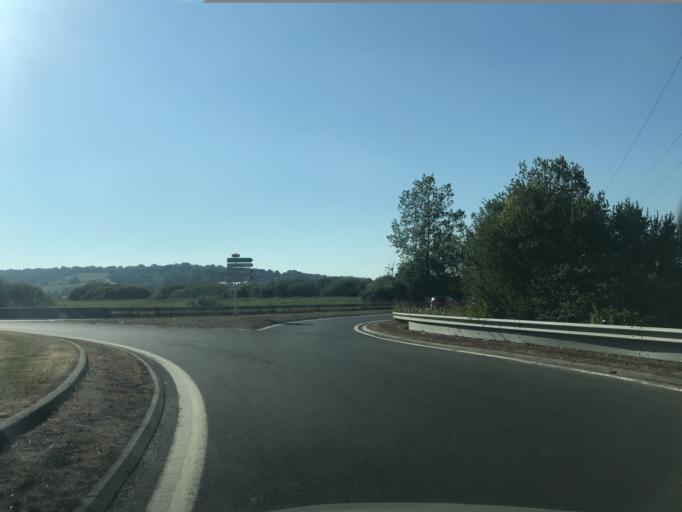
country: FR
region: Lower Normandy
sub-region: Departement du Calvados
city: Touques
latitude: 49.3318
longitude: 0.1067
